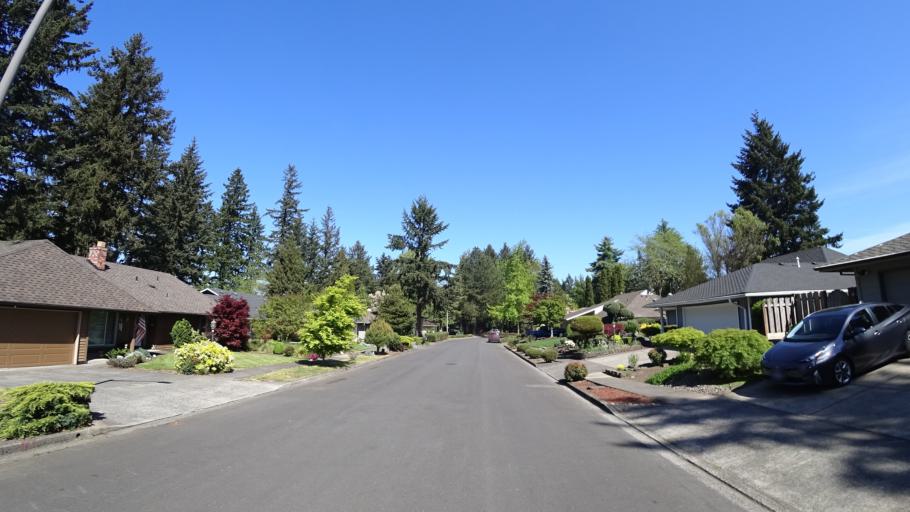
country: US
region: Oregon
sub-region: Washington County
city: Aloha
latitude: 45.4792
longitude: -122.8388
